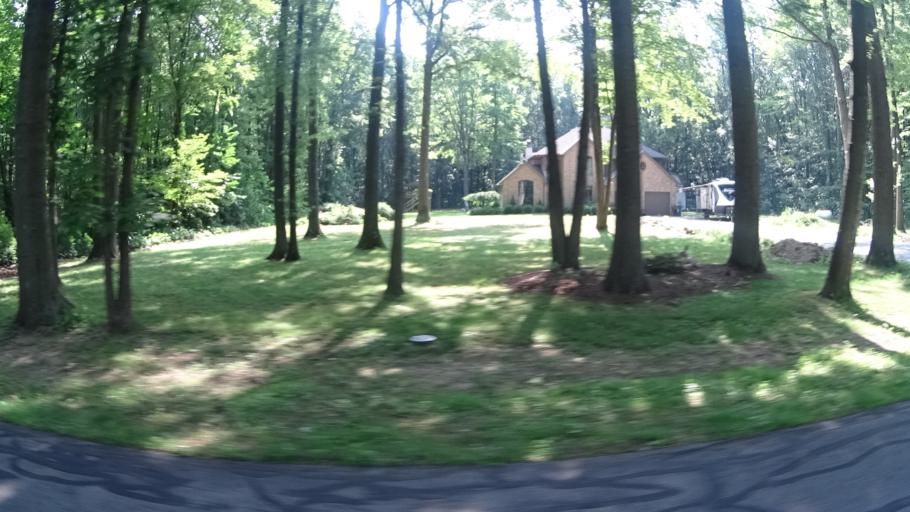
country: US
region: Ohio
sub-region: Lorain County
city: Vermilion
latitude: 41.3674
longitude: -82.4304
